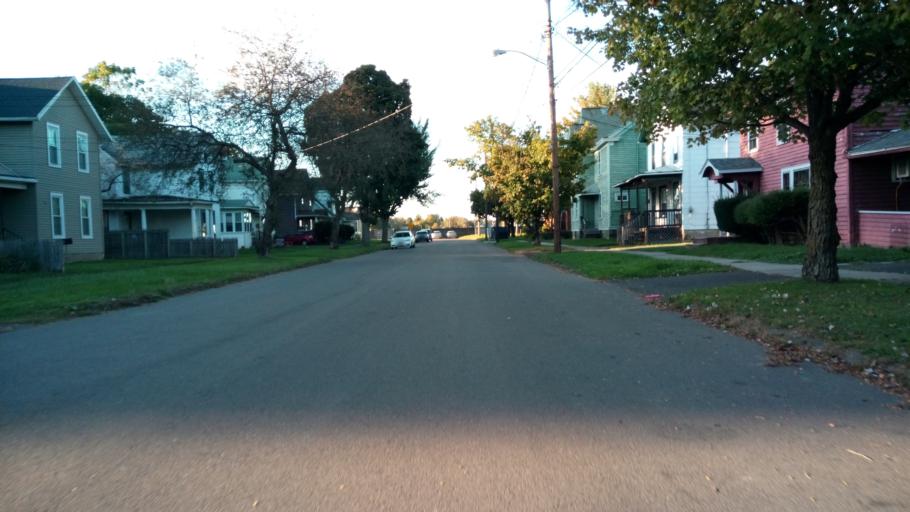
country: US
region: New York
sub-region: Chemung County
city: Elmira
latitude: 42.0831
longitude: -76.8091
